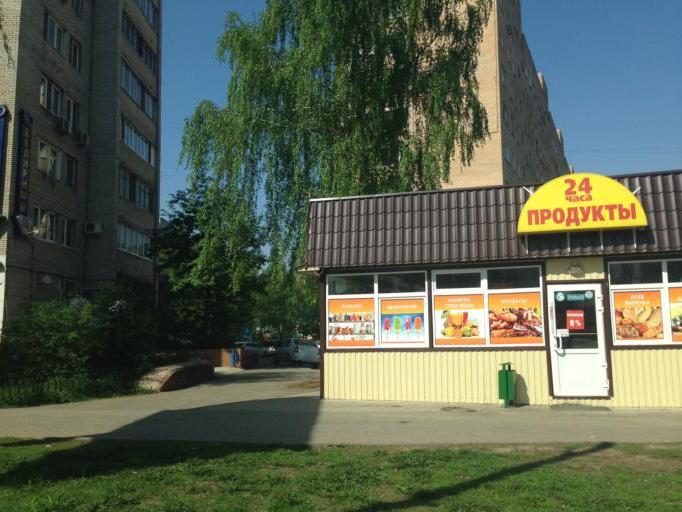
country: RU
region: Moskovskaya
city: Balashikha
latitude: 55.8175
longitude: 37.9666
